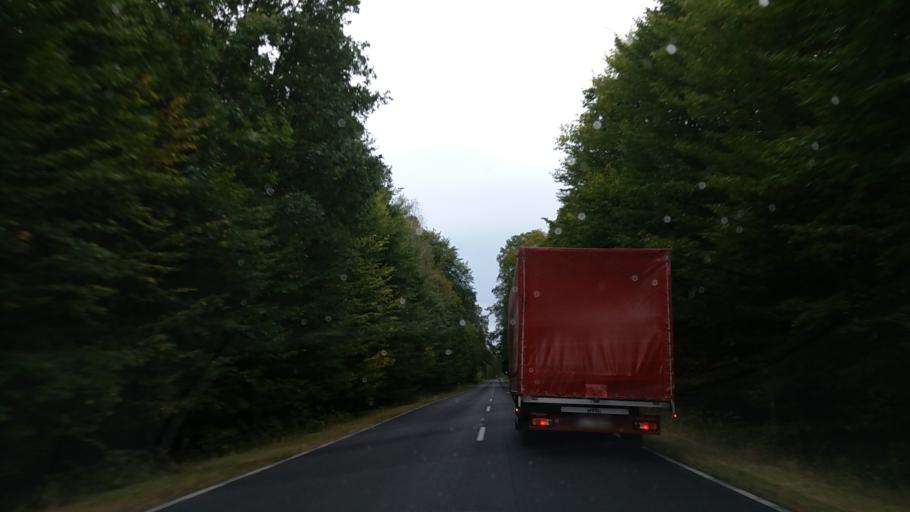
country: PL
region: West Pomeranian Voivodeship
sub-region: Powiat mysliborski
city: Barlinek
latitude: 52.9251
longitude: 15.1940
